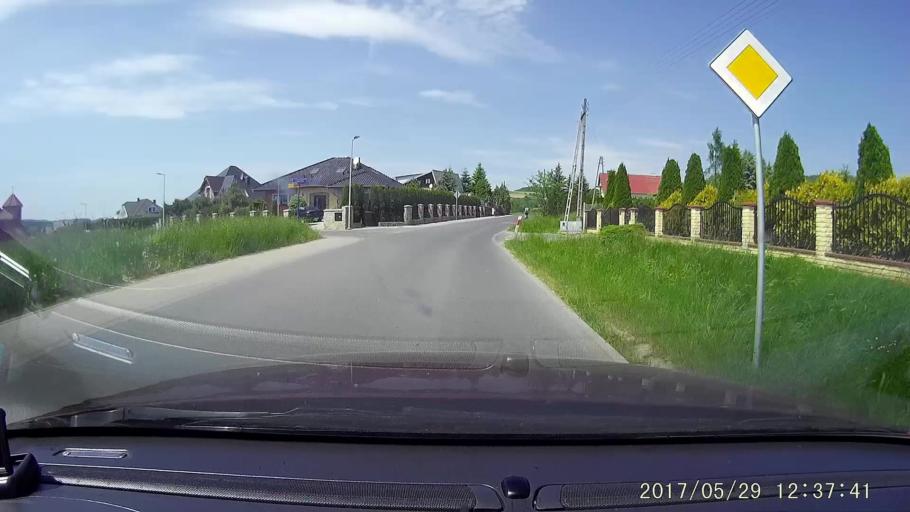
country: PL
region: Lower Silesian Voivodeship
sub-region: Powiat jeleniogorski
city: Jezow Sudecki
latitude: 50.9273
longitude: 15.7482
